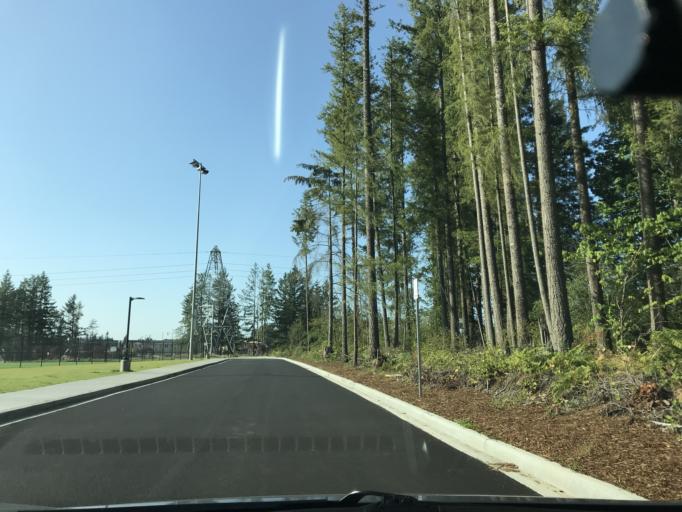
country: US
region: Washington
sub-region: King County
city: Ravensdale
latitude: 47.3567
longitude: -122.0213
